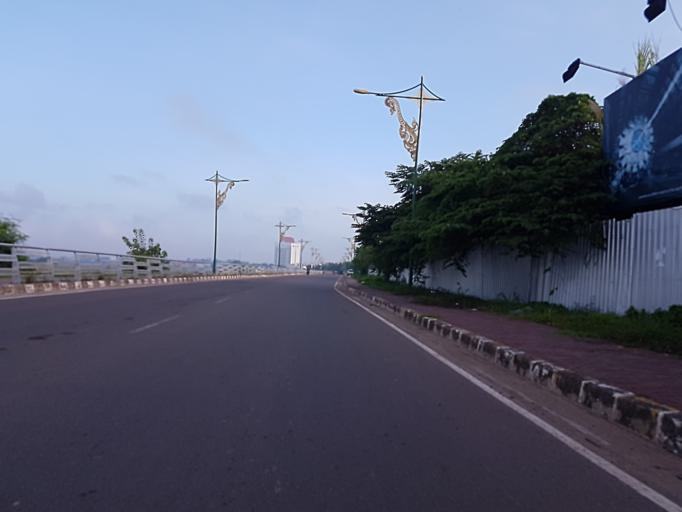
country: LA
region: Vientiane
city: Vientiane
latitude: 17.9453
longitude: 102.6160
